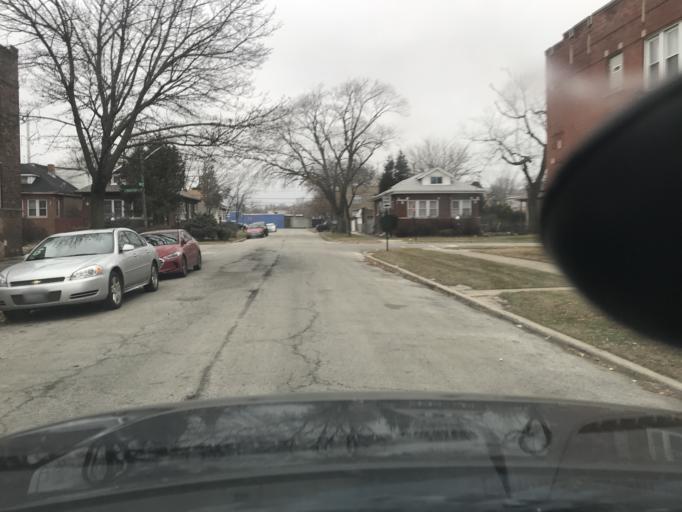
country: US
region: Indiana
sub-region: Lake County
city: Whiting
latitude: 41.7426
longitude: -87.5704
